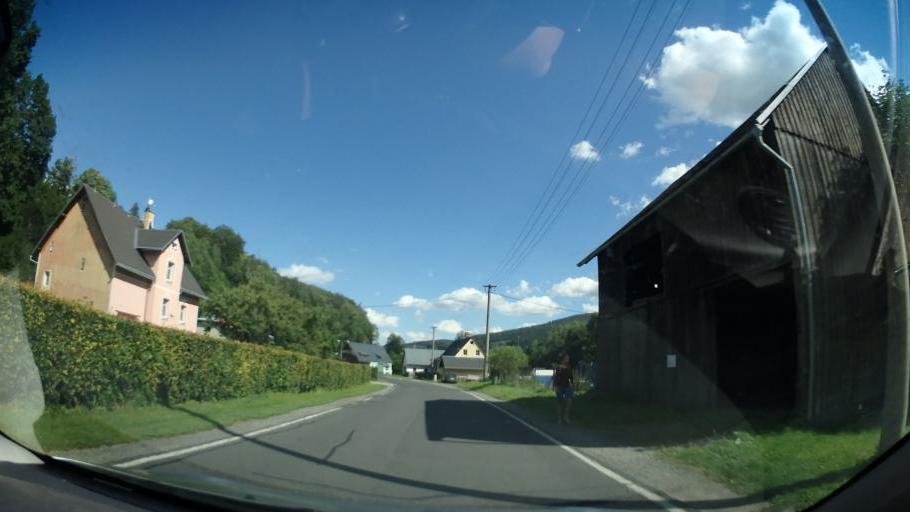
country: CZ
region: Olomoucky
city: Vapenna
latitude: 50.2242
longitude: 17.0943
